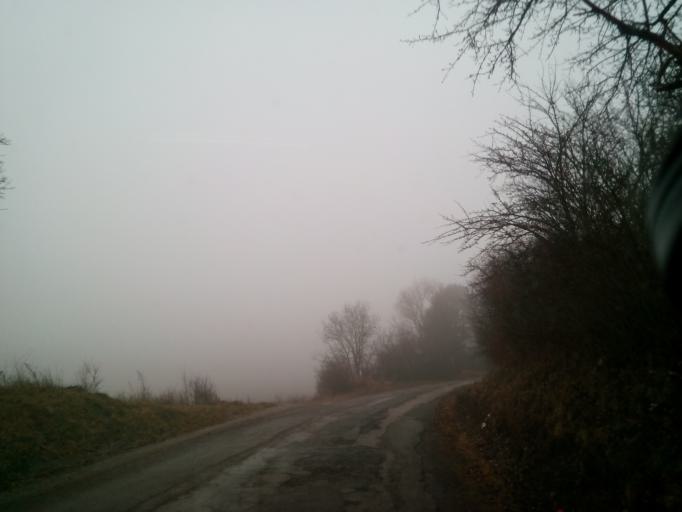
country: SK
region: Presovsky
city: Spisske Podhradie
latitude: 49.0313
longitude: 20.7978
